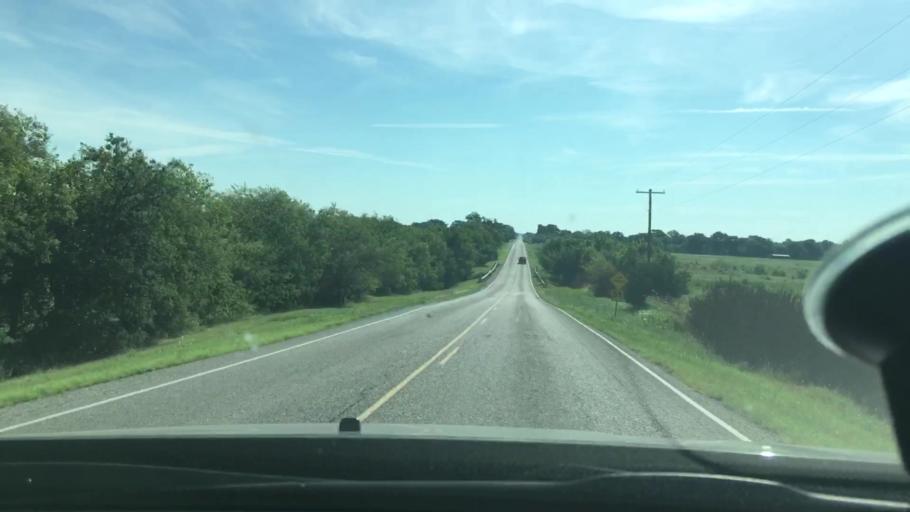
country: US
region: Oklahoma
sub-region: Carter County
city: Lone Grove
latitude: 34.3327
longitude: -97.2124
